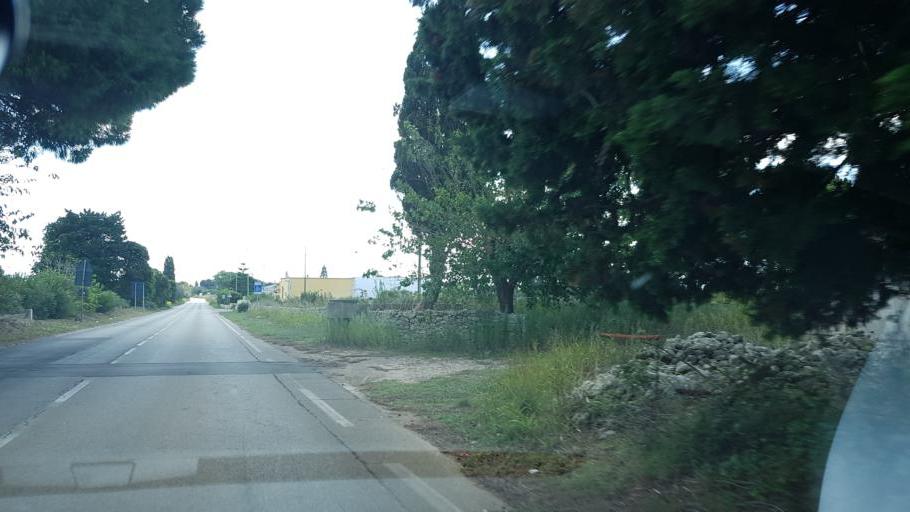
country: IT
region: Apulia
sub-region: Provincia di Lecce
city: Borgagne
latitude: 40.2349
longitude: 18.4439
